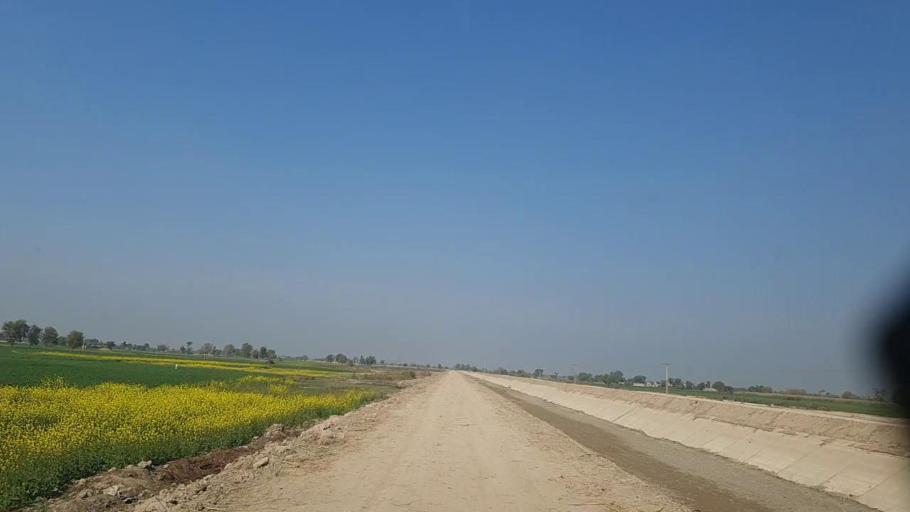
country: PK
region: Sindh
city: Sakrand
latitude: 26.1548
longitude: 68.3292
